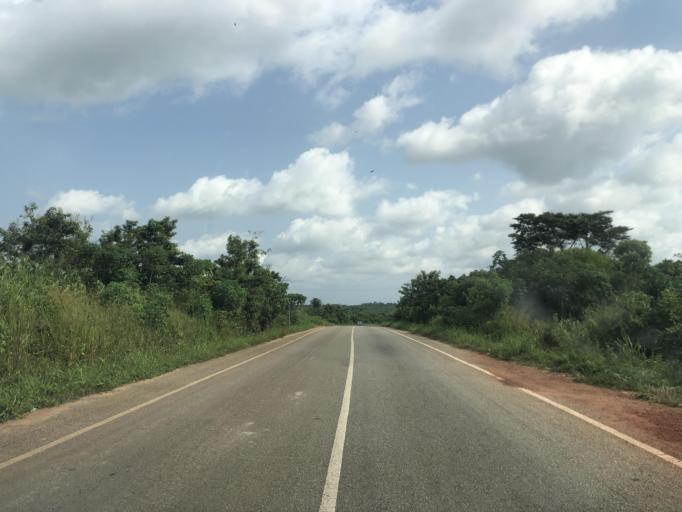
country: GH
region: Central
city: Elmina
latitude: 5.2103
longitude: -1.3226
